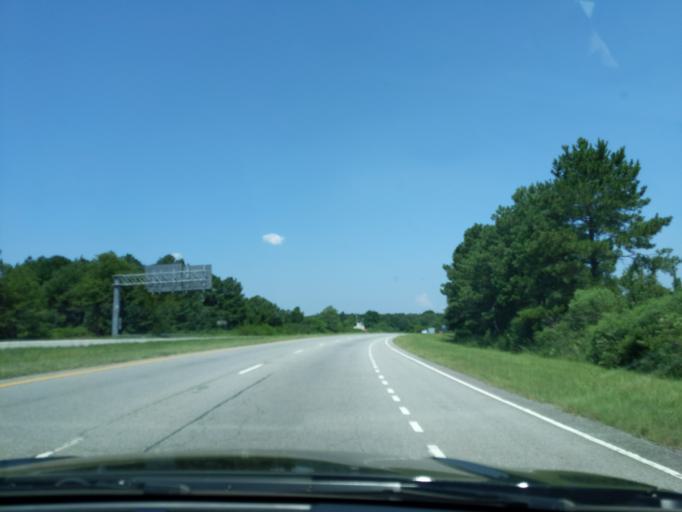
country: US
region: South Carolina
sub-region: Richland County
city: Forest Acres
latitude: 33.9518
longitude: -80.9767
